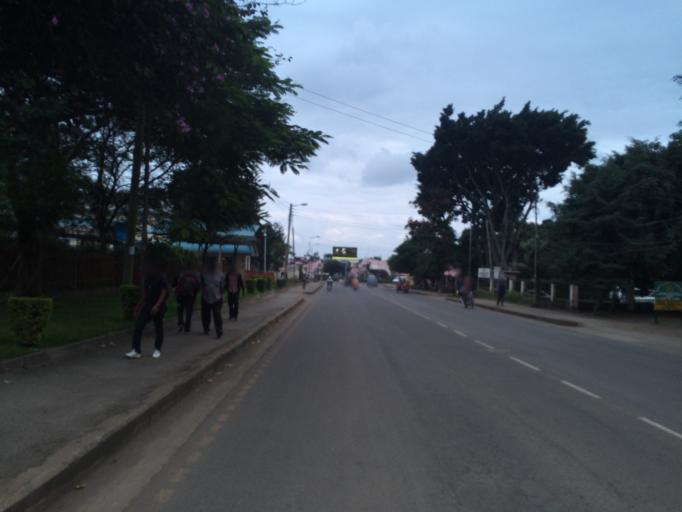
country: TZ
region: Arusha
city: Arusha
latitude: -3.3686
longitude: 36.6950
